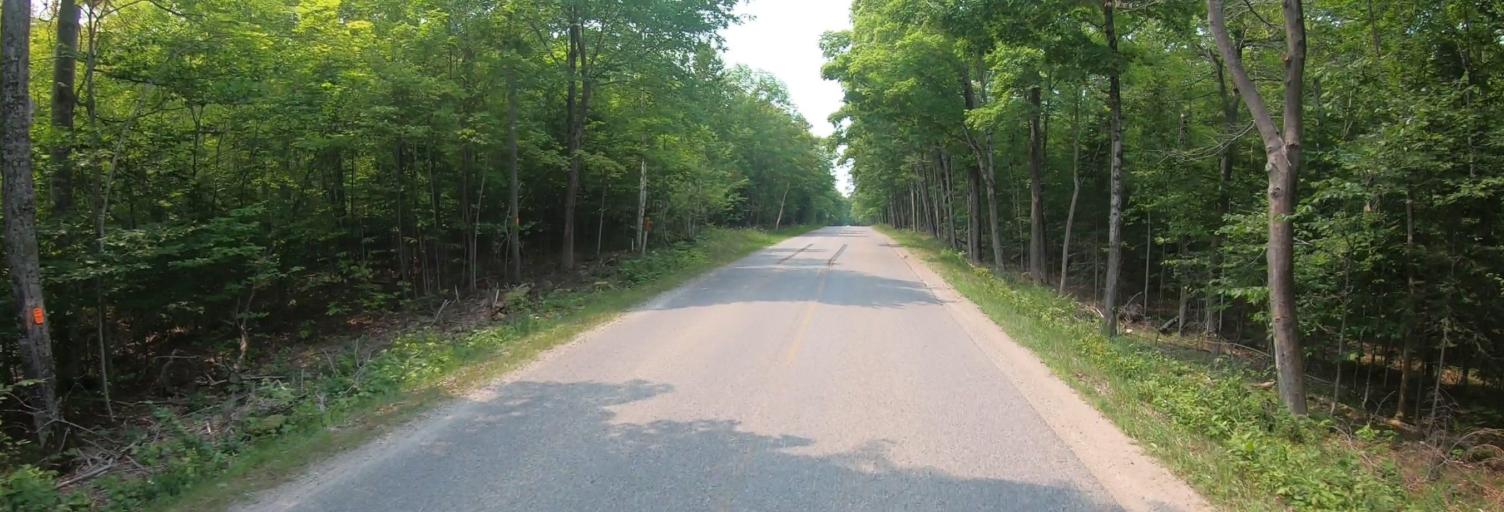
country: CA
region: Ontario
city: Thessalon
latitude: 46.0131
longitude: -83.6934
